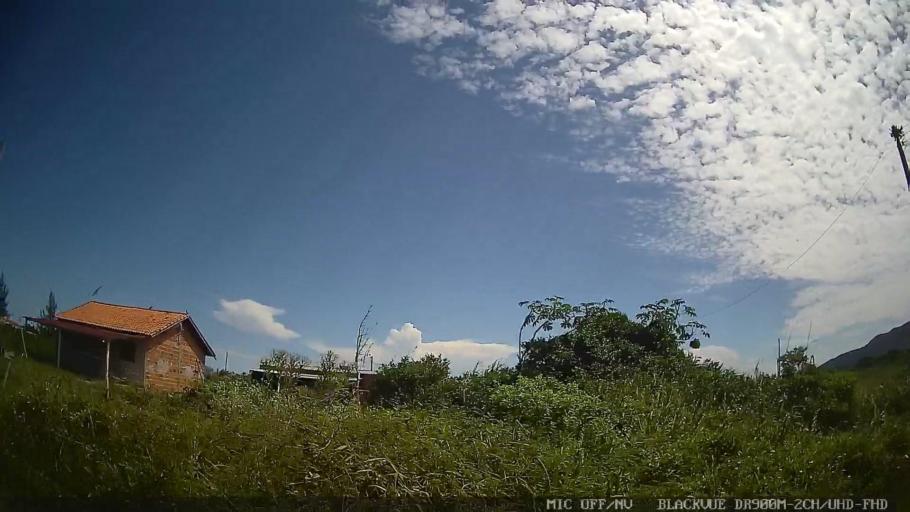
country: BR
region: Sao Paulo
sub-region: Iguape
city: Iguape
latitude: -24.7242
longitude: -47.5121
